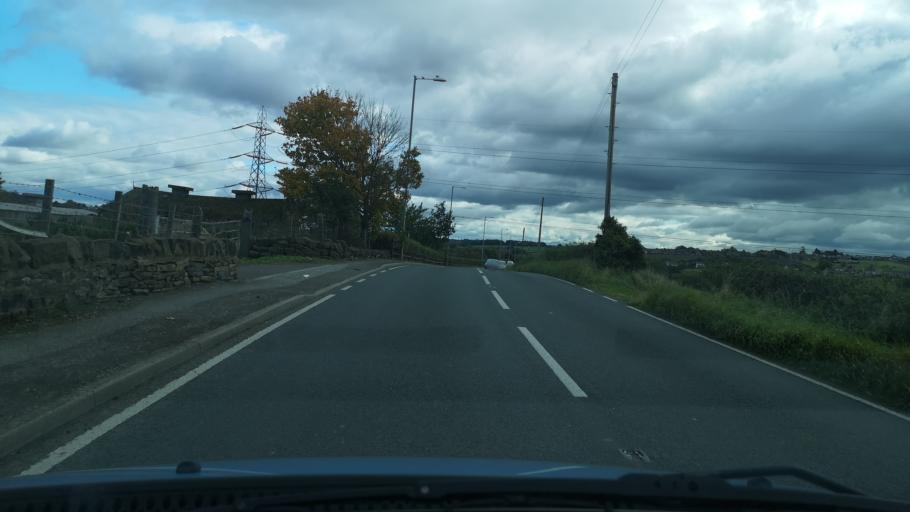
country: GB
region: England
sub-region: City and Borough of Wakefield
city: Middlestown
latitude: 53.6608
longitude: -1.5914
